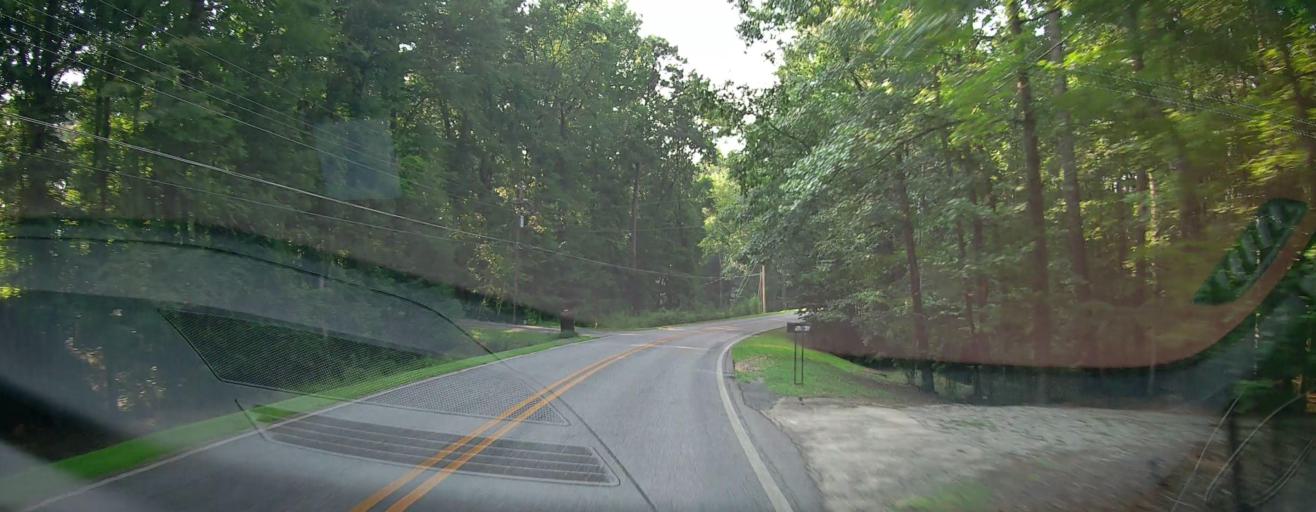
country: US
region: Georgia
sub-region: Bibb County
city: Macon
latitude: 32.9508
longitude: -83.7309
